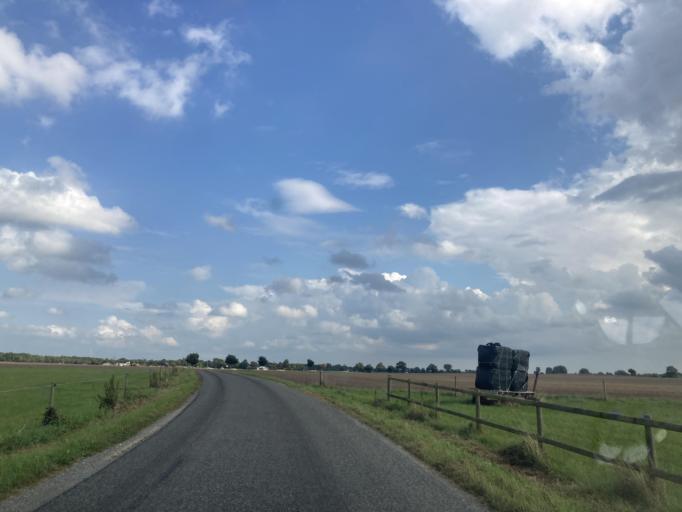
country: DK
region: Zealand
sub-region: Roskilde Kommune
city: Svogerslev
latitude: 55.6103
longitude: 12.0281
